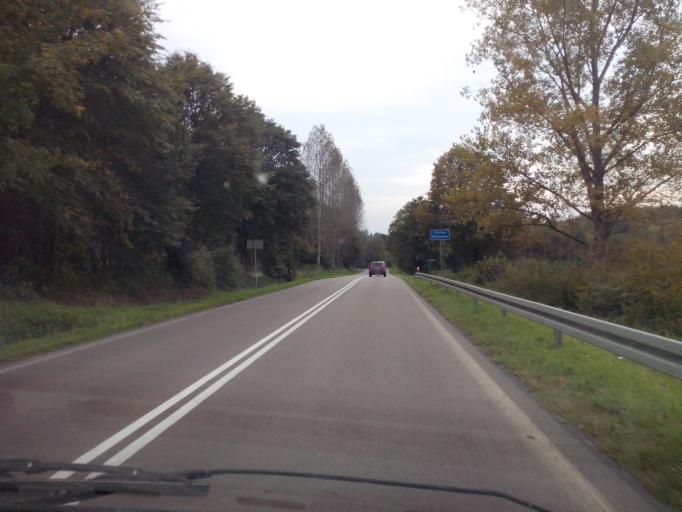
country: PL
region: Subcarpathian Voivodeship
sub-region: Powiat przemyski
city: Nienadowa
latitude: 49.8240
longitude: 22.4537
